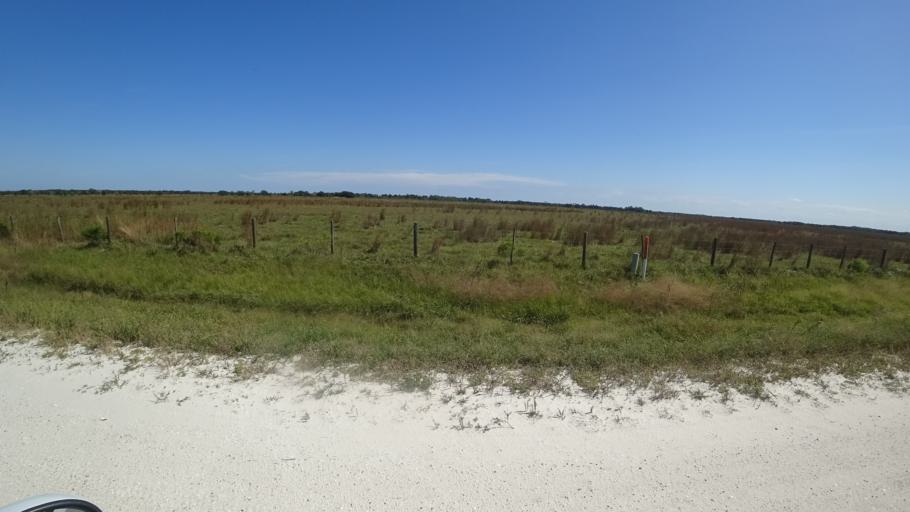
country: US
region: Florida
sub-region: DeSoto County
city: Arcadia
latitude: 27.3095
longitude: -82.0805
